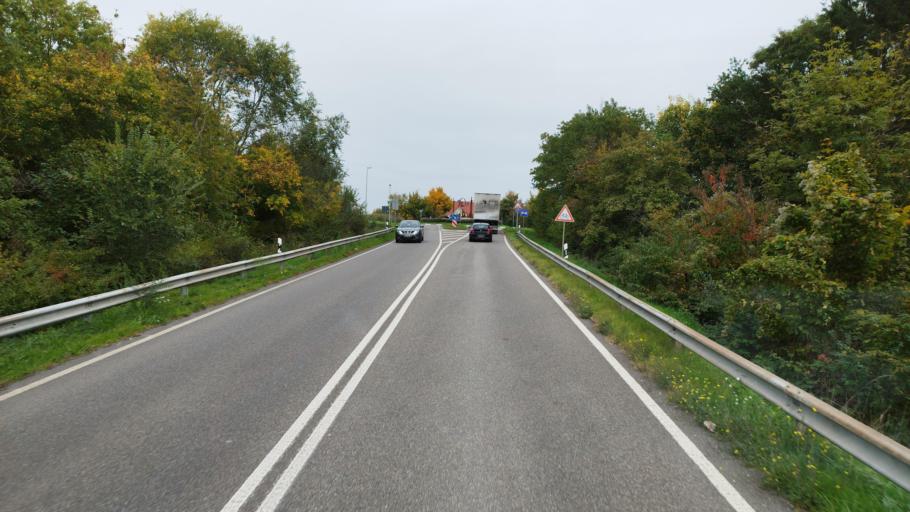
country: DE
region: Rheinland-Pfalz
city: Neupotz
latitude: 49.1221
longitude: 8.3085
